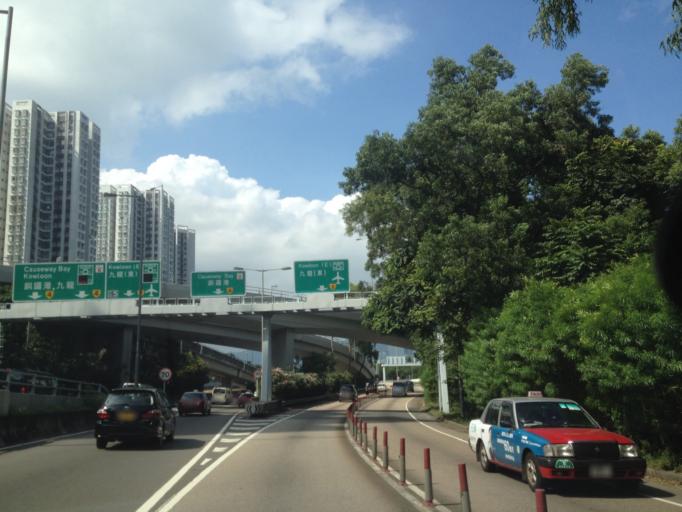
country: HK
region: Wanchai
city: Wan Chai
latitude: 22.2848
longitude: 114.2216
